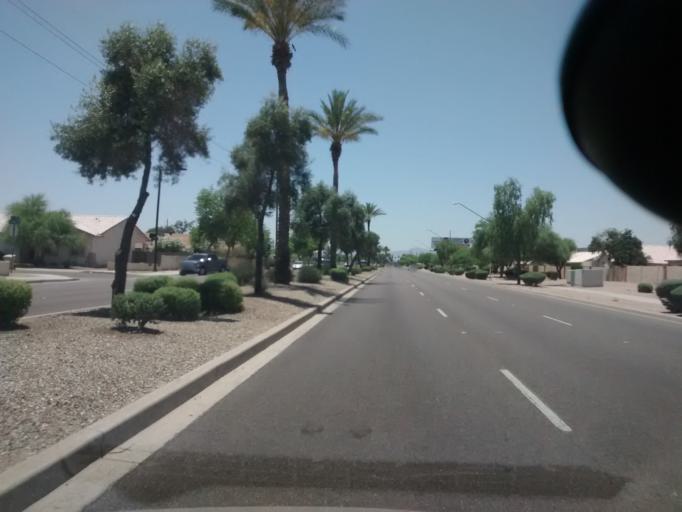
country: US
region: Arizona
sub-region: Maricopa County
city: Peoria
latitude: 33.5378
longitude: -112.2339
